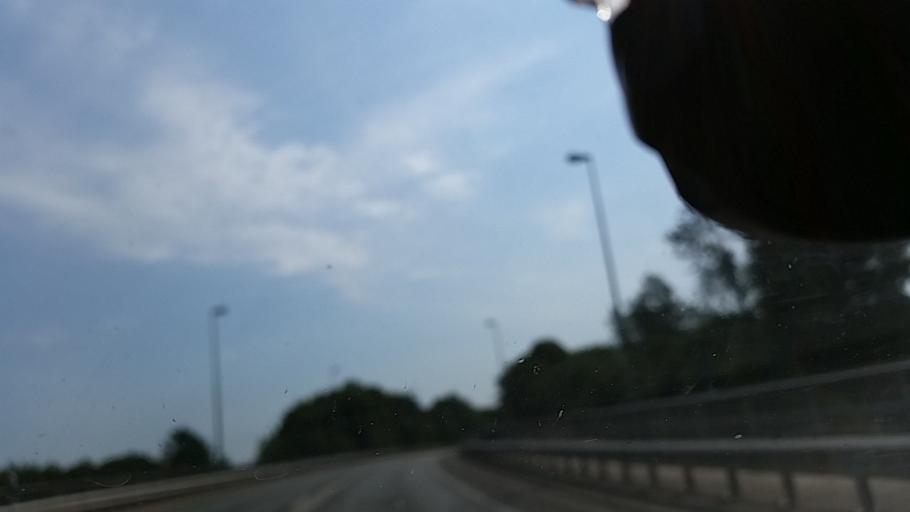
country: DE
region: Lower Saxony
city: Diepholz
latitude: 52.6113
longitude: 8.3861
